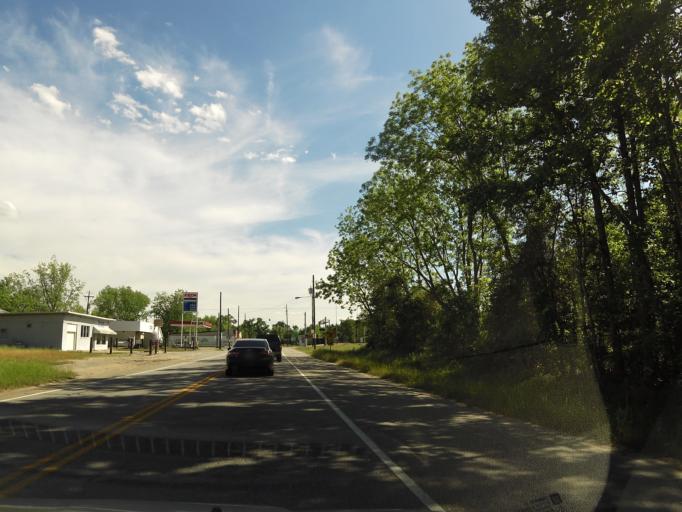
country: US
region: South Carolina
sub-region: Bamberg County
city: Denmark
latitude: 33.1823
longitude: -81.1845
